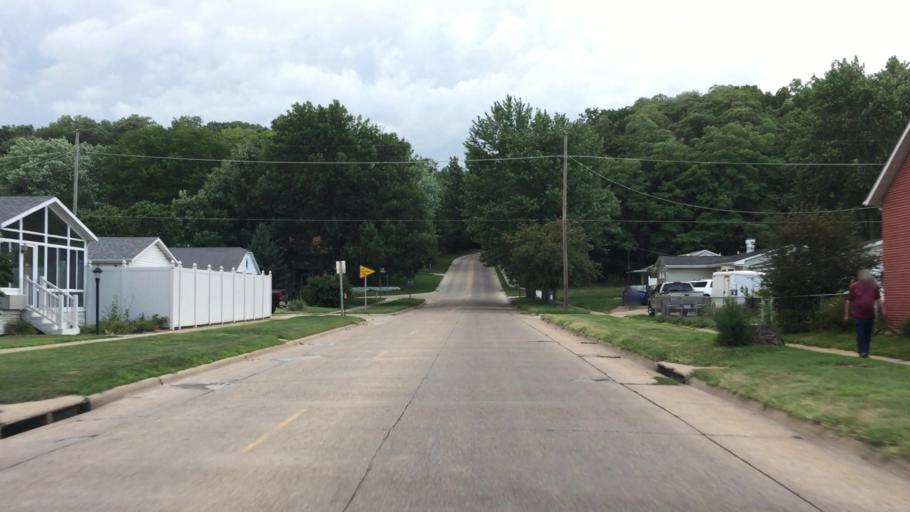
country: US
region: Iowa
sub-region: Lee County
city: Fort Madison
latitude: 40.6353
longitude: -91.3245
